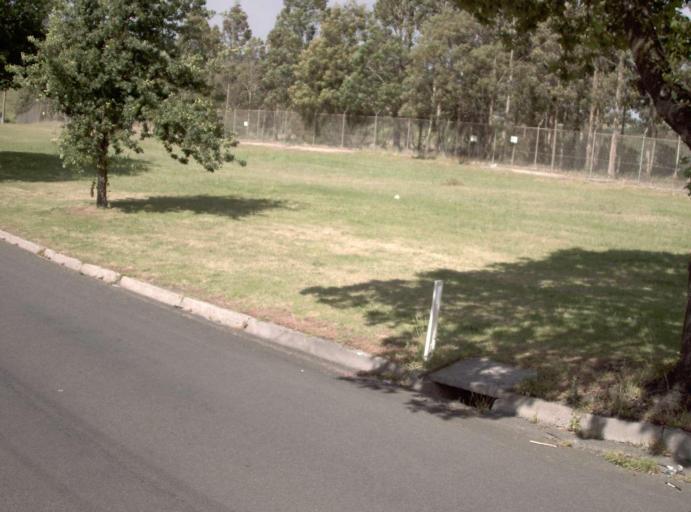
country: AU
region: Victoria
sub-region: Latrobe
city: Morwell
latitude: -38.1624
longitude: 146.3673
